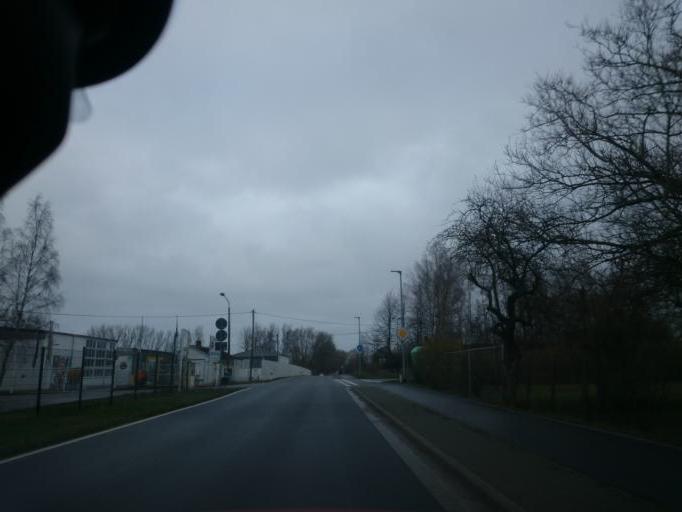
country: DE
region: Mecklenburg-Vorpommern
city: Lambrechtshagen
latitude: 54.1242
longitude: 12.0330
